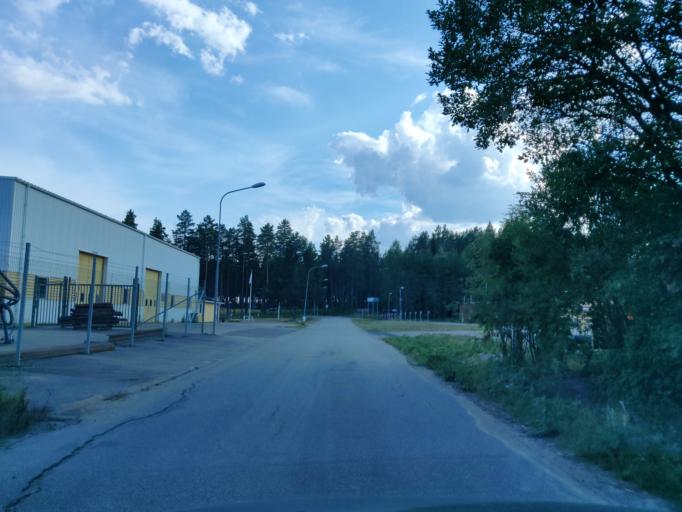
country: SE
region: Vaermland
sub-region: Hagfors Kommun
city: Hagfors
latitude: 60.0134
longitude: 13.6712
